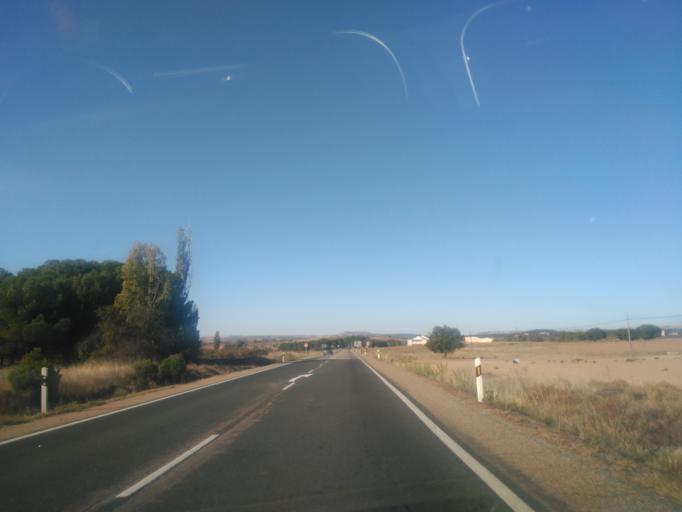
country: ES
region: Castille and Leon
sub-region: Provincia de Burgos
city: Valdezate
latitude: 41.6152
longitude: -3.9226
